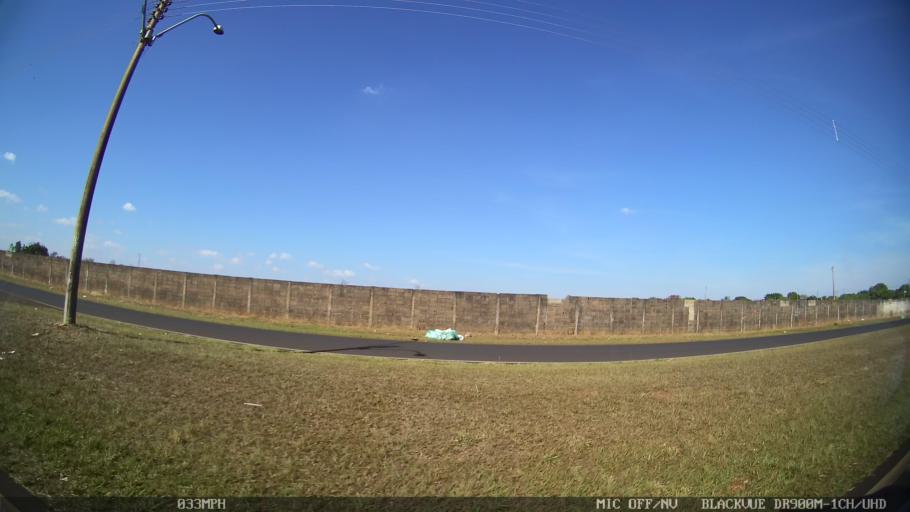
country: BR
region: Sao Paulo
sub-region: Ribeirao Preto
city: Ribeirao Preto
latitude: -21.1477
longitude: -47.7708
